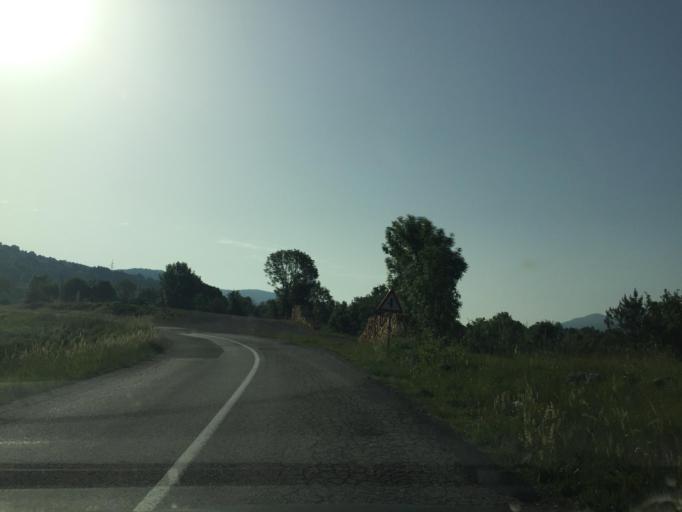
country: HR
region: Primorsko-Goranska
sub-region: Grad Opatija
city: Opatija
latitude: 45.4557
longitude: 14.1639
